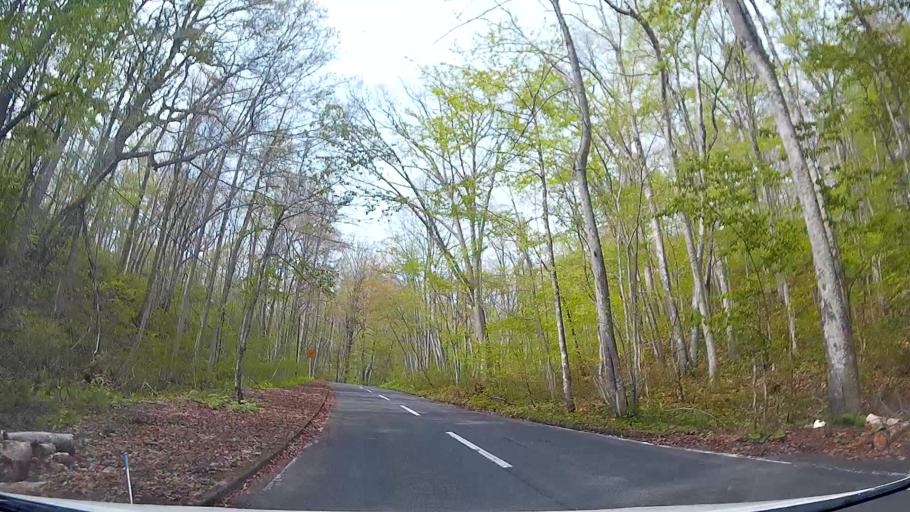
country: JP
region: Akita
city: Hanawa
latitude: 40.4301
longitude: 140.9148
